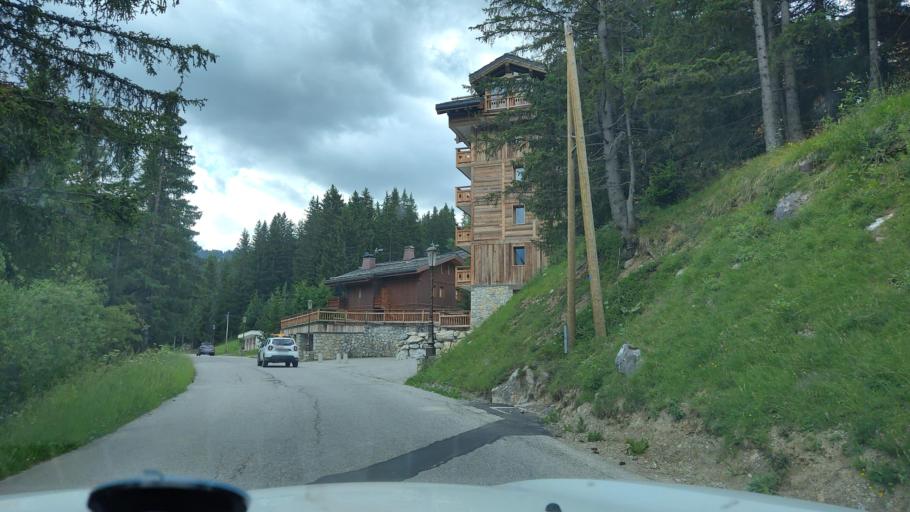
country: FR
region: Rhone-Alpes
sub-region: Departement de la Savoie
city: Courchevel
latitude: 45.4124
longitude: 6.6583
